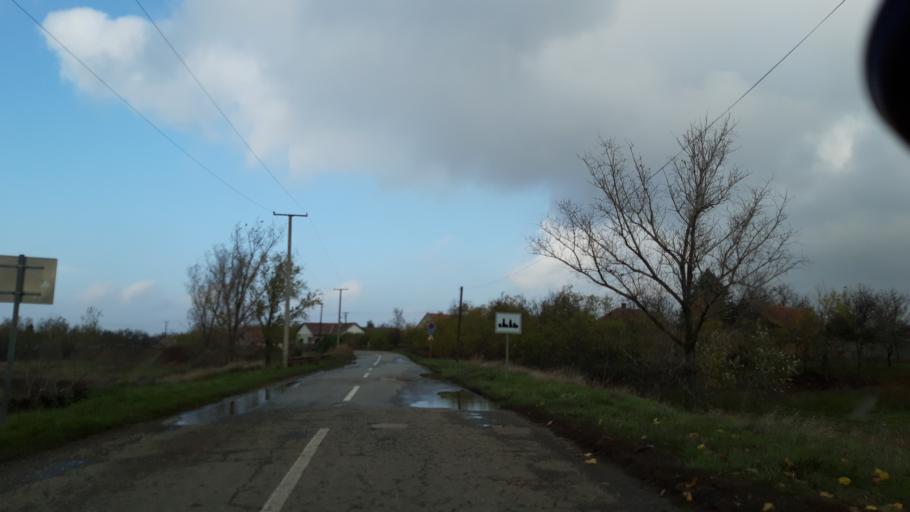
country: RS
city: Padej
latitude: 45.8189
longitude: 20.1586
